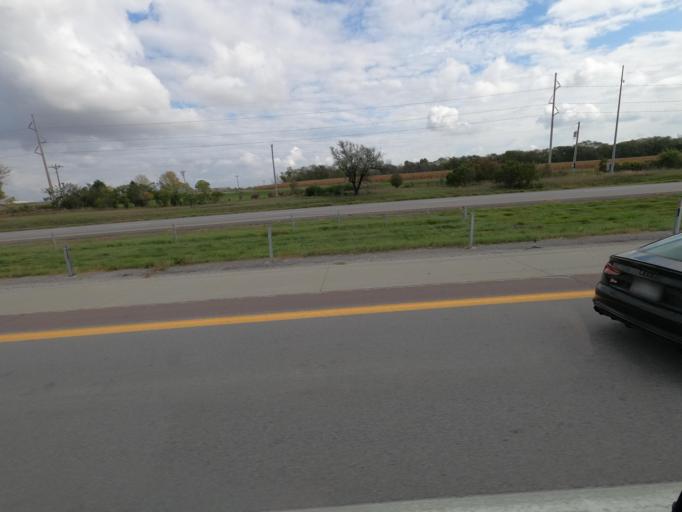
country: US
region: Iowa
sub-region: Story County
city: Huxley
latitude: 41.9498
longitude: -93.5700
